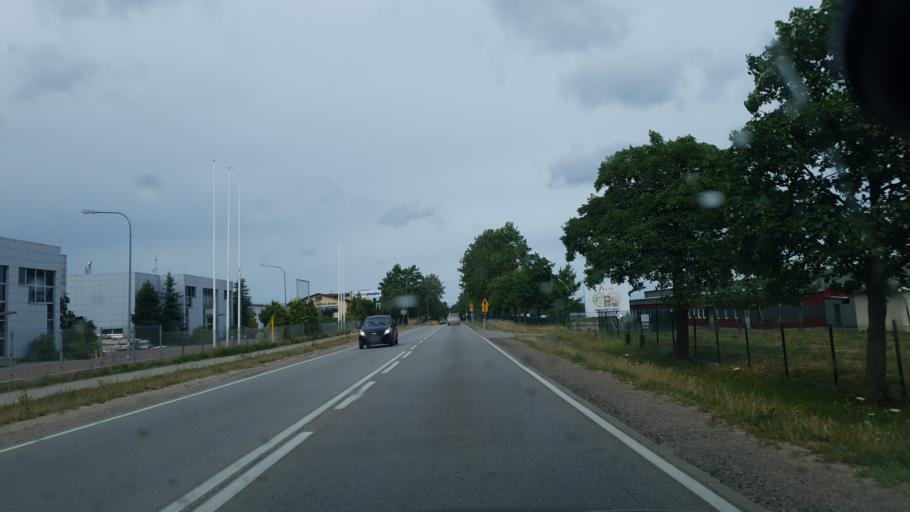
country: PL
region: Pomeranian Voivodeship
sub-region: Powiat kartuski
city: Banino
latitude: 54.4203
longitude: 18.3801
